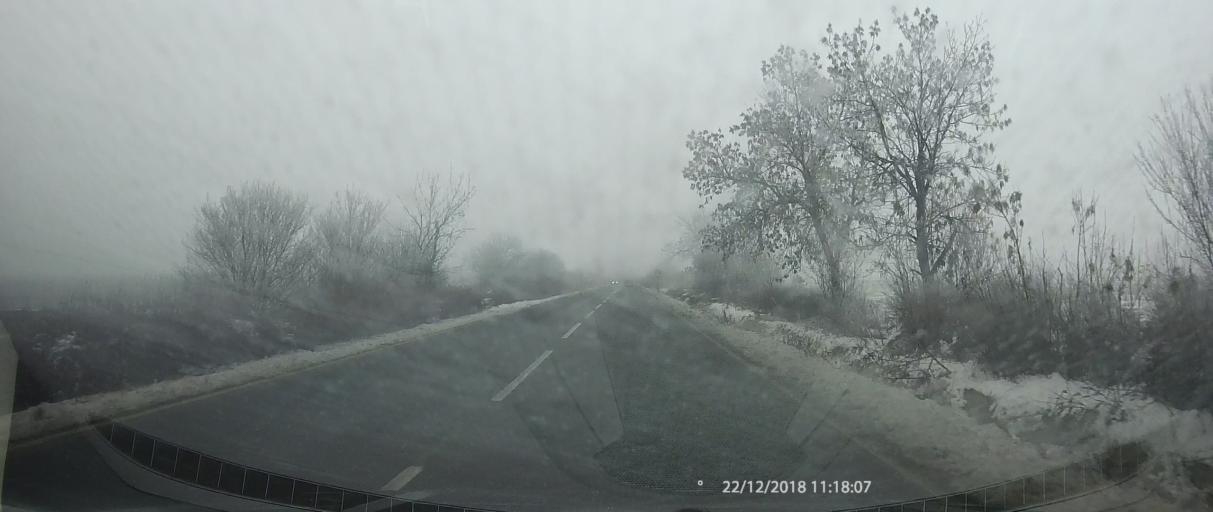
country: BG
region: Kyustendil
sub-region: Obshtina Kyustendil
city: Kyustendil
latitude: 42.2726
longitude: 22.7684
